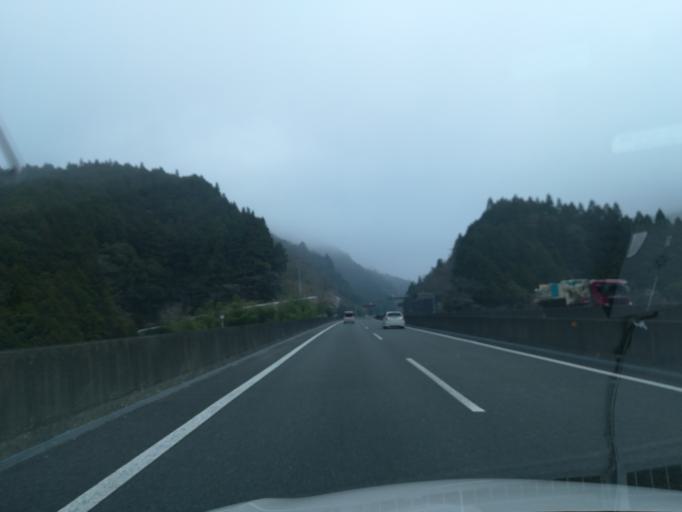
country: JP
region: Ehime
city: Kawanoecho
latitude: 33.7777
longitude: 133.6607
